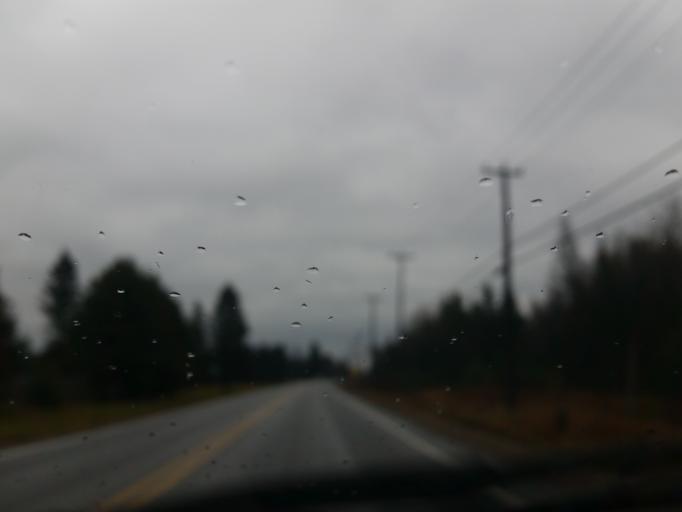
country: CA
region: Quebec
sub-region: Capitale-Nationale
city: Shannon
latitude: 46.8854
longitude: -71.4946
